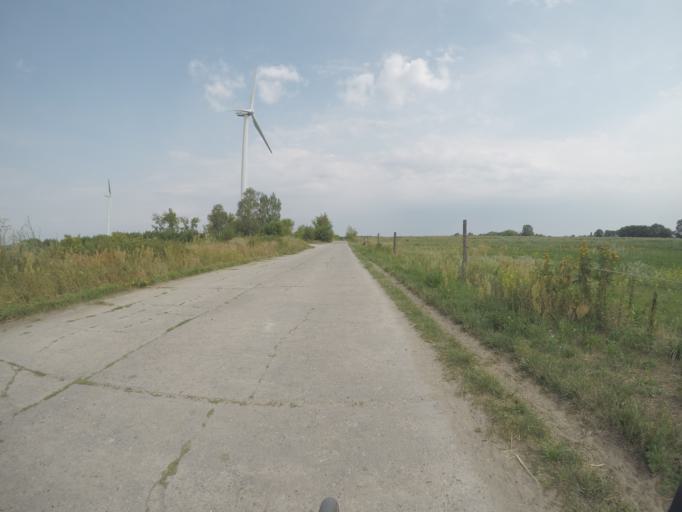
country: DE
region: Berlin
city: Blankenfelde
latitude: 52.6641
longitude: 13.4263
